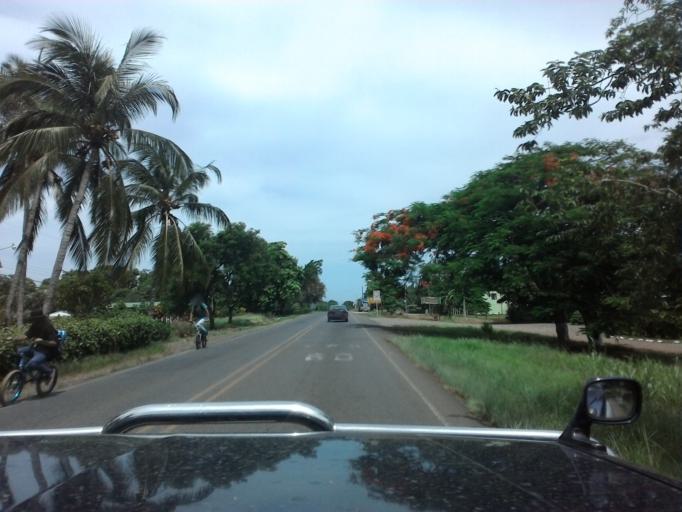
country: CR
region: Puntarenas
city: Esparza
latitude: 9.9998
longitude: -84.6484
